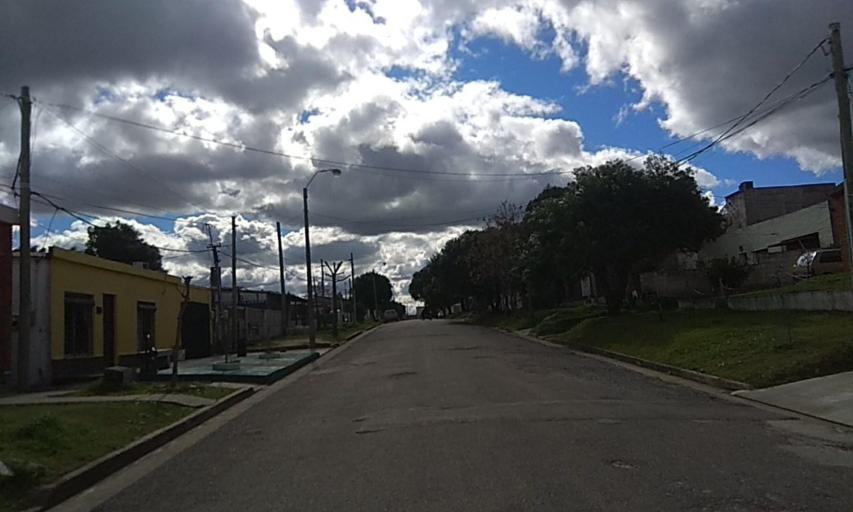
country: UY
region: Florida
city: Florida
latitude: -34.0900
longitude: -56.2302
